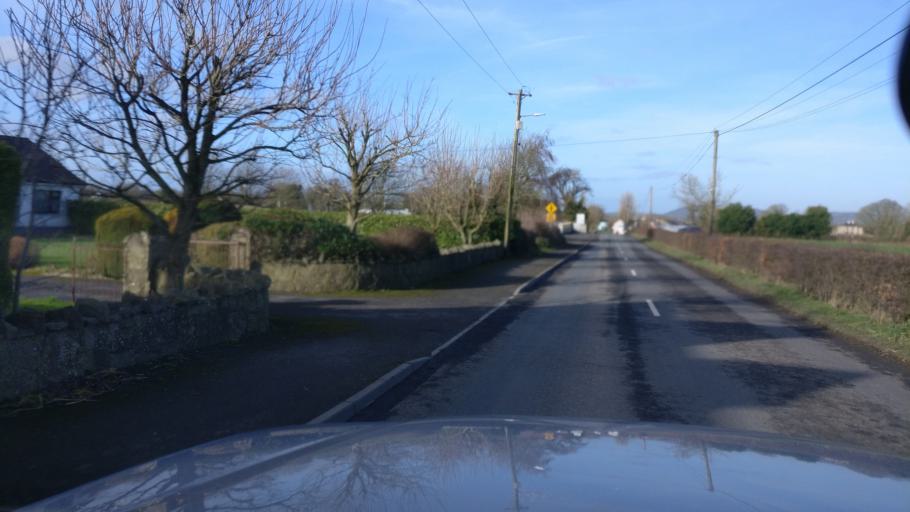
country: IE
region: Leinster
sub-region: Laois
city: Stradbally
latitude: 52.9574
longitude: -7.1997
